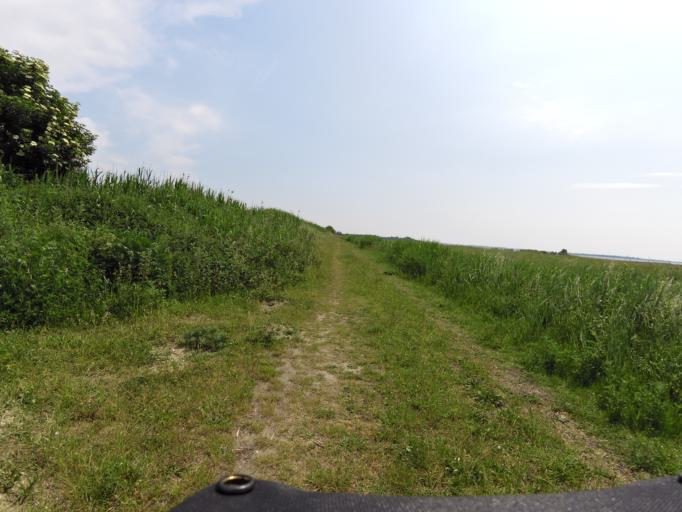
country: NL
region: North Brabant
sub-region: Gemeente Bergen op Zoom
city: Bergen op Zoom
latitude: 51.4883
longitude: 4.2491
